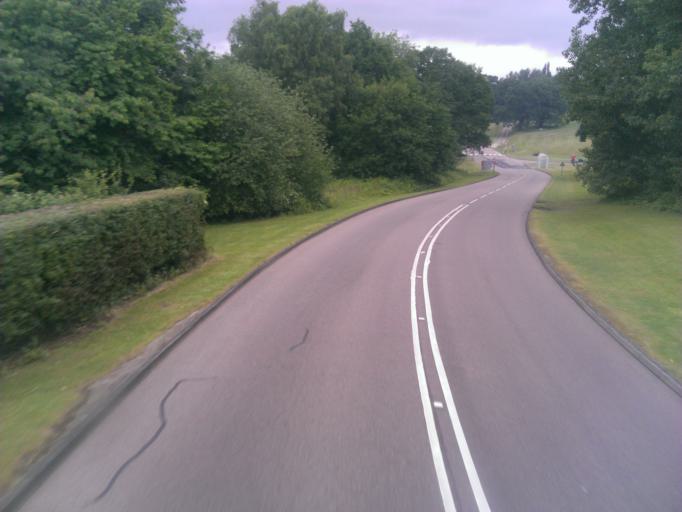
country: GB
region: England
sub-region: Essex
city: Rowhedge
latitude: 51.8740
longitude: 0.9419
